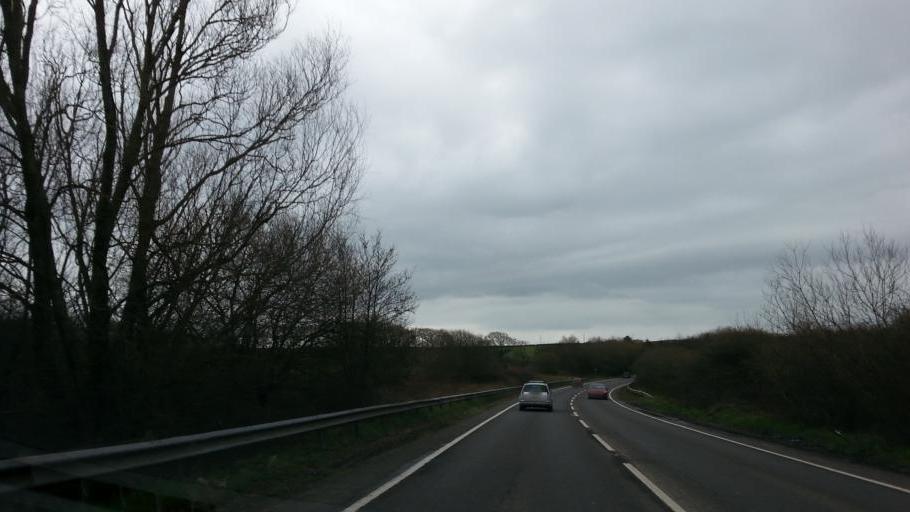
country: GB
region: England
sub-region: Devon
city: Fremington
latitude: 51.0454
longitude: -4.1273
